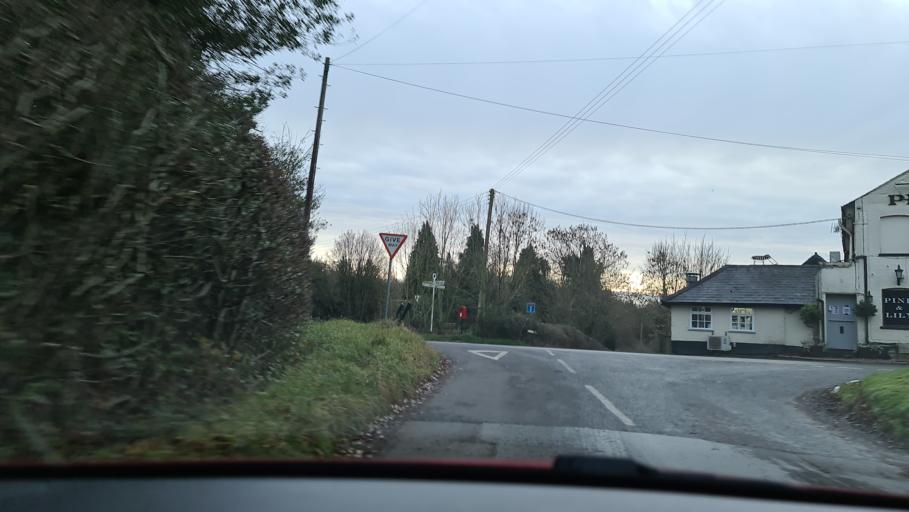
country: GB
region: England
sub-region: Buckinghamshire
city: Princes Risborough
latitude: 51.7101
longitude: -0.8049
